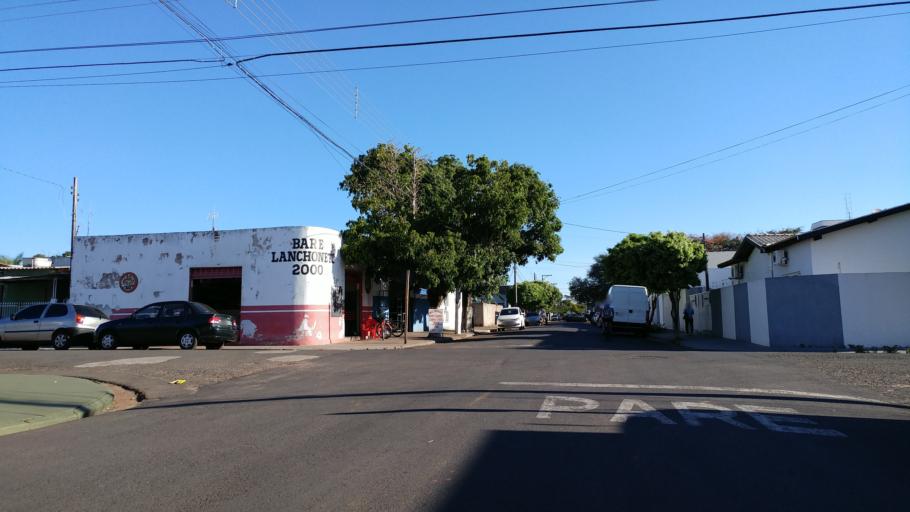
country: BR
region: Sao Paulo
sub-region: Paraguacu Paulista
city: Paraguacu Paulista
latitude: -22.4249
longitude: -50.5817
